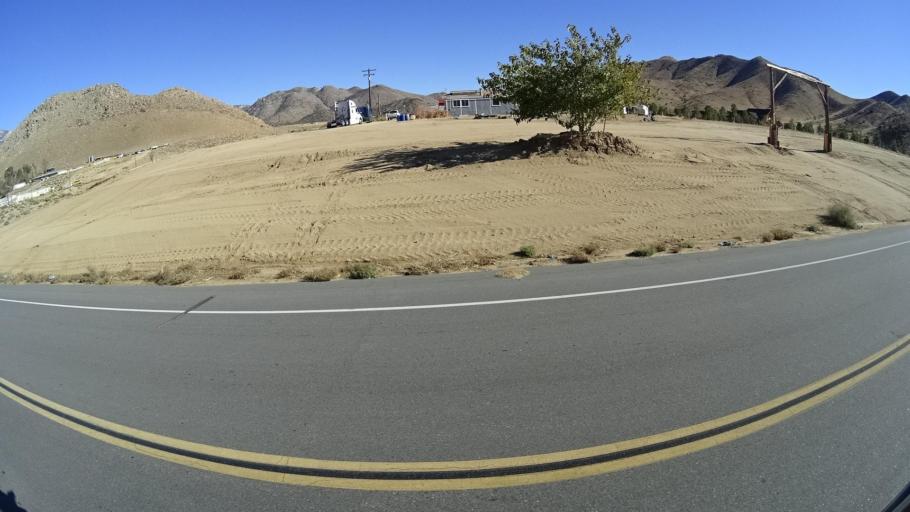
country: US
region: California
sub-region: Kern County
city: Wofford Heights
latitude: 35.7064
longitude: -118.4235
